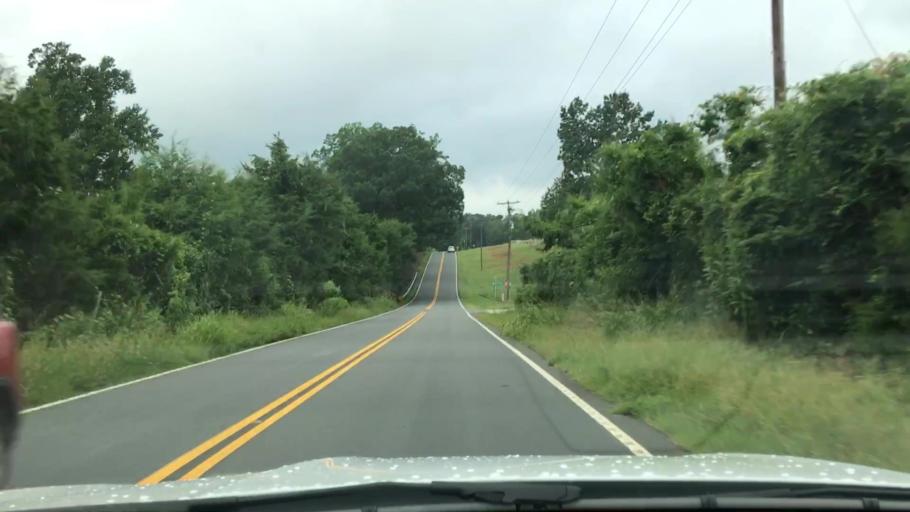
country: US
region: South Carolina
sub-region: Spartanburg County
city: Roebuck
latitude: 34.8210
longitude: -81.9336
